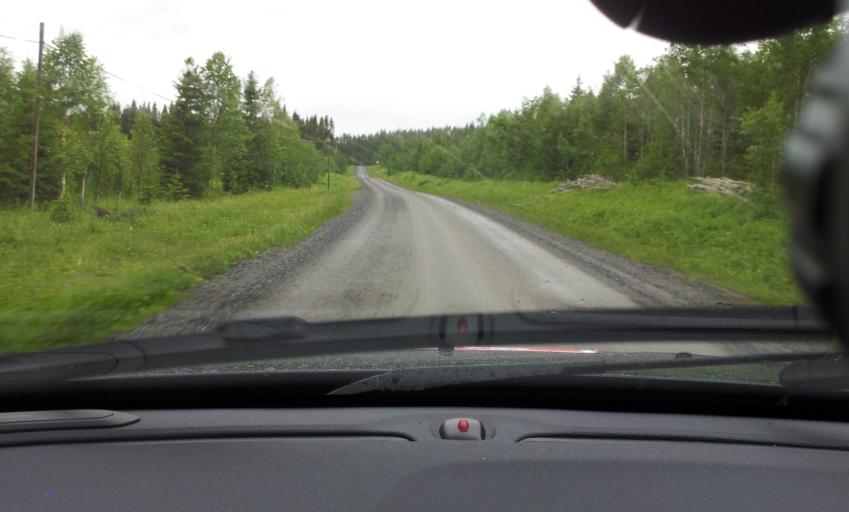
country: SE
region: Jaemtland
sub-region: Are Kommun
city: Are
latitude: 63.4827
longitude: 12.7939
